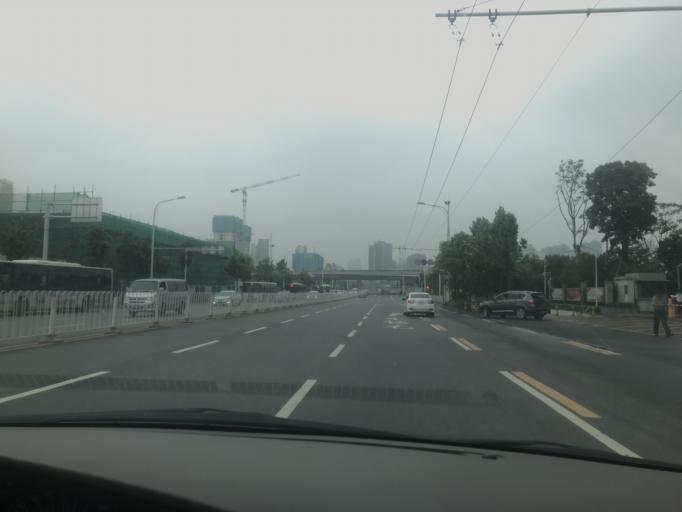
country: CN
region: Hubei
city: Yongfeng
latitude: 30.5567
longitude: 114.2348
